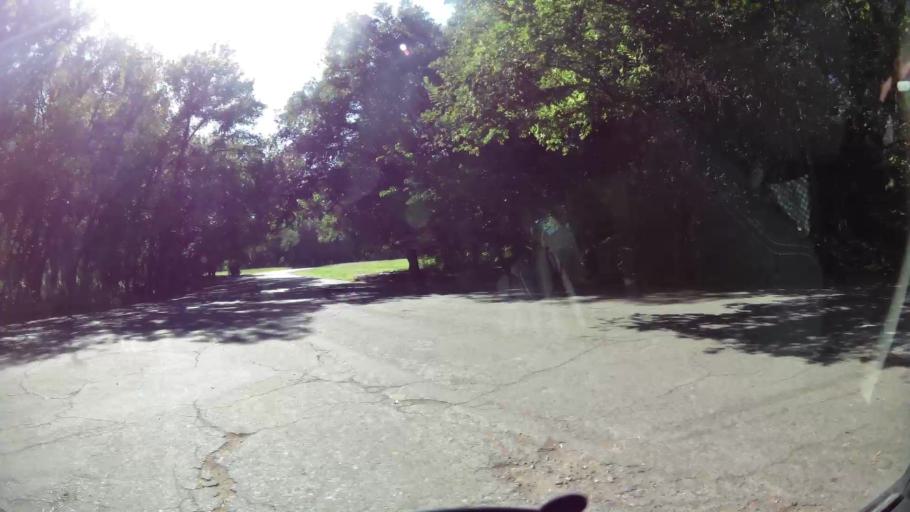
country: AR
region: Mendoza
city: Mendoza
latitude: -32.8862
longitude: -68.8694
